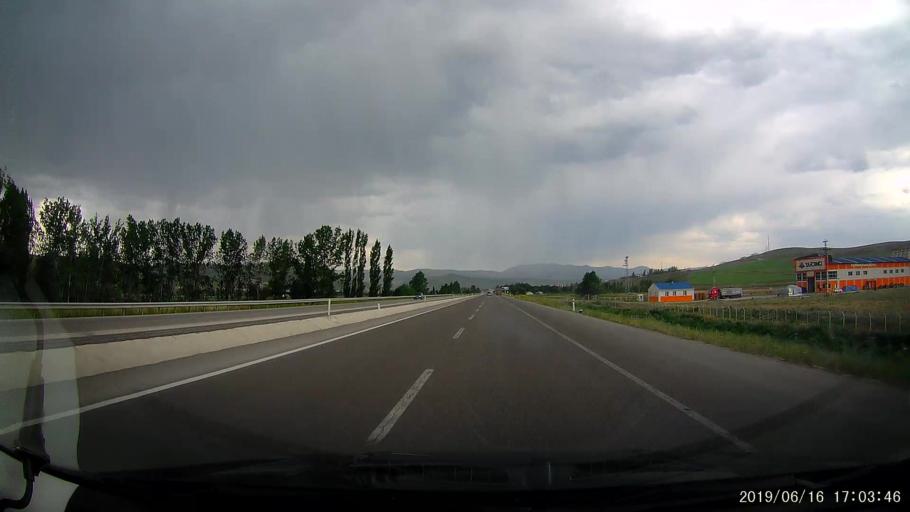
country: TR
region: Erzurum
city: Askale
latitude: 39.9332
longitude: 40.7240
